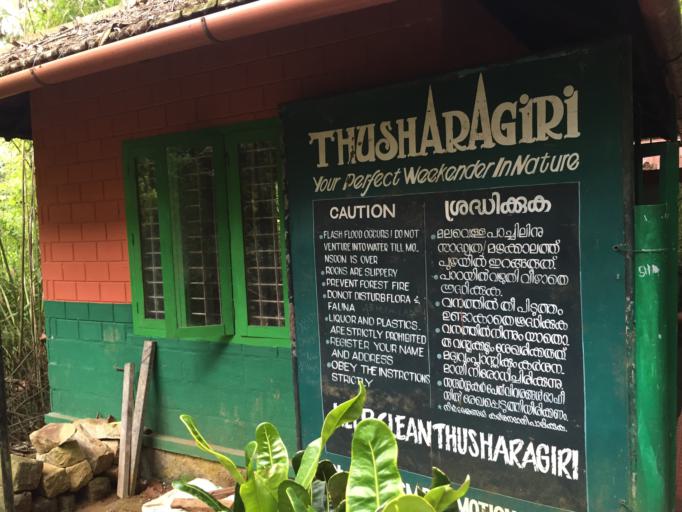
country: IN
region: Kerala
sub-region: Wayanad
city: Kalpetta
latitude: 11.4718
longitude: 76.0523
